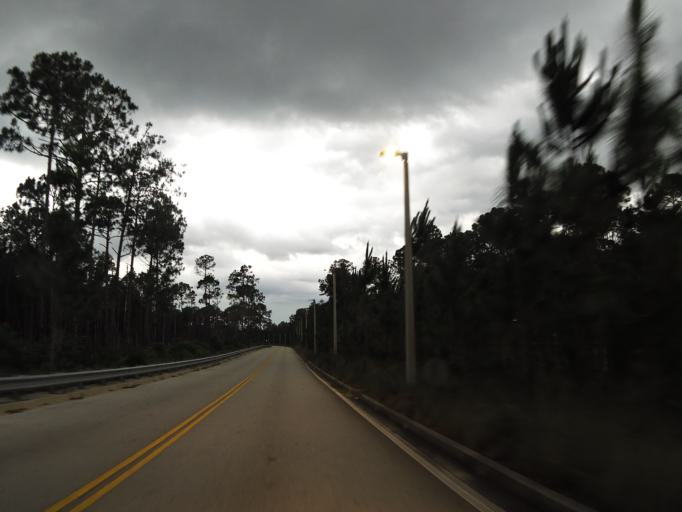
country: US
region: Florida
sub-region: Duval County
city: Jacksonville Beach
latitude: 30.2722
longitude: -81.5137
